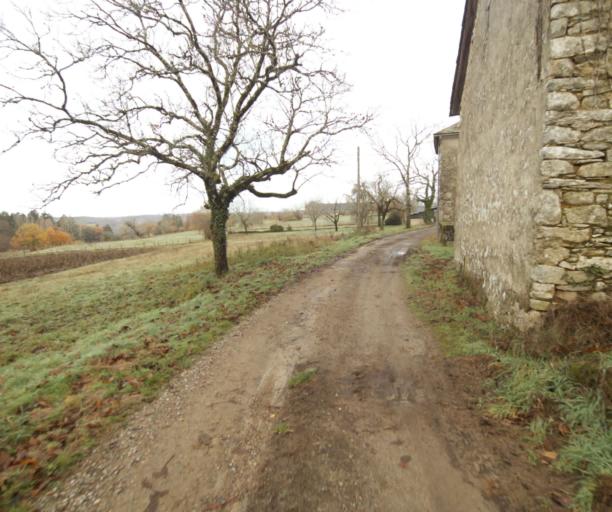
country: FR
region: Limousin
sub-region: Departement de la Correze
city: Cornil
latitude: 45.2035
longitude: 1.7199
